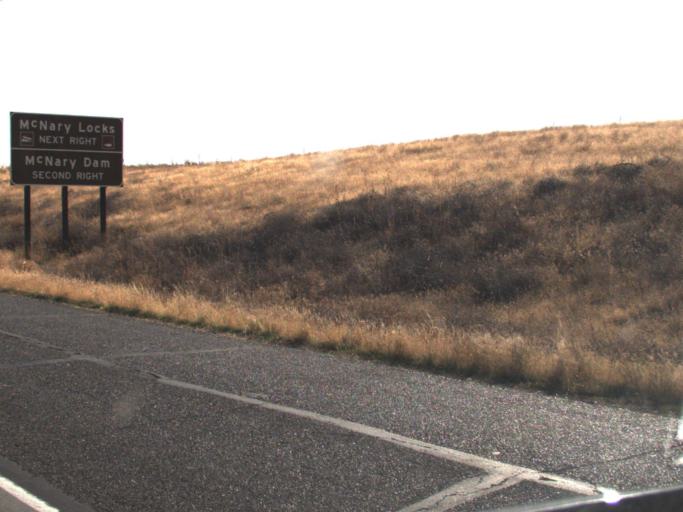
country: US
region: Oregon
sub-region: Umatilla County
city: Umatilla
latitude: 45.9522
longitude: -119.3387
